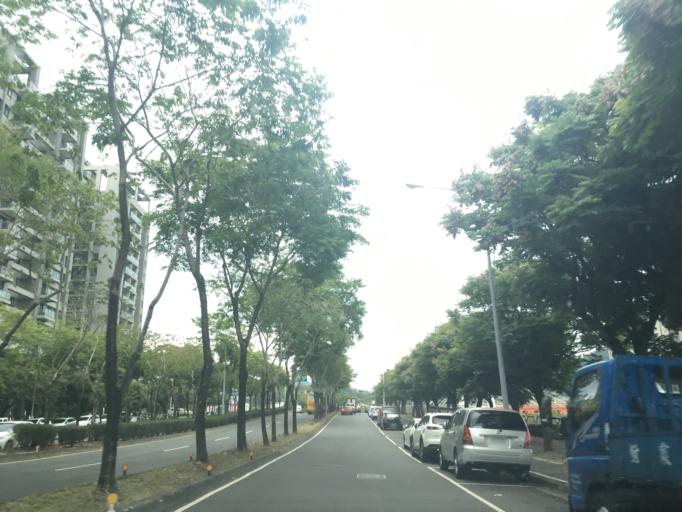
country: TW
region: Taiwan
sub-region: Taichung City
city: Taichung
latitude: 24.1609
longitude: 120.7313
